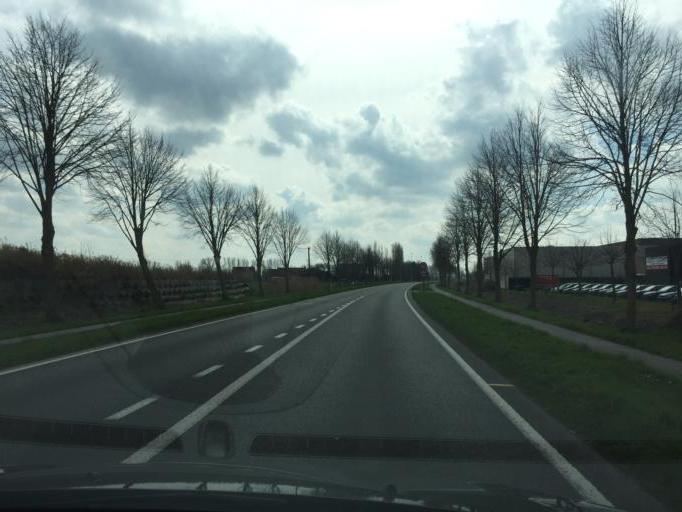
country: BE
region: Flanders
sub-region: Provincie West-Vlaanderen
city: Ruiselede
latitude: 51.0447
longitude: 3.4118
